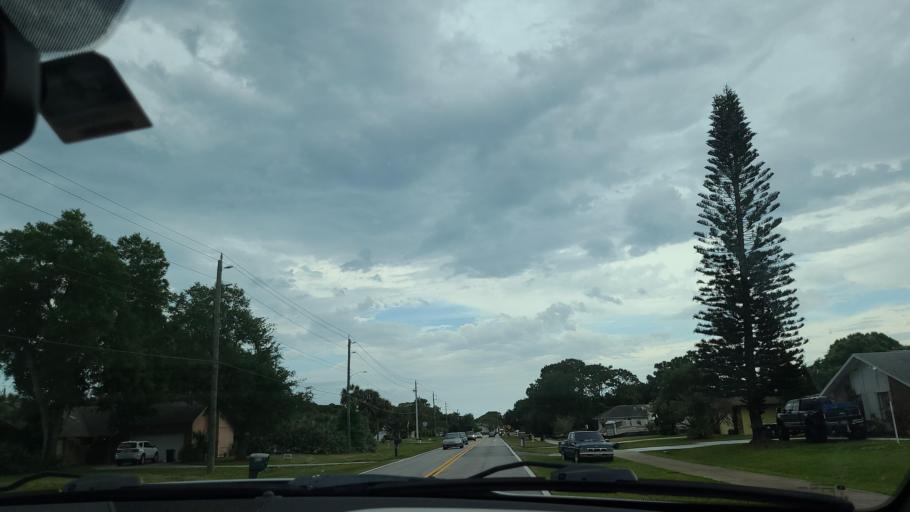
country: US
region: Florida
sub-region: Brevard County
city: West Melbourne
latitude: 28.0176
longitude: -80.6522
